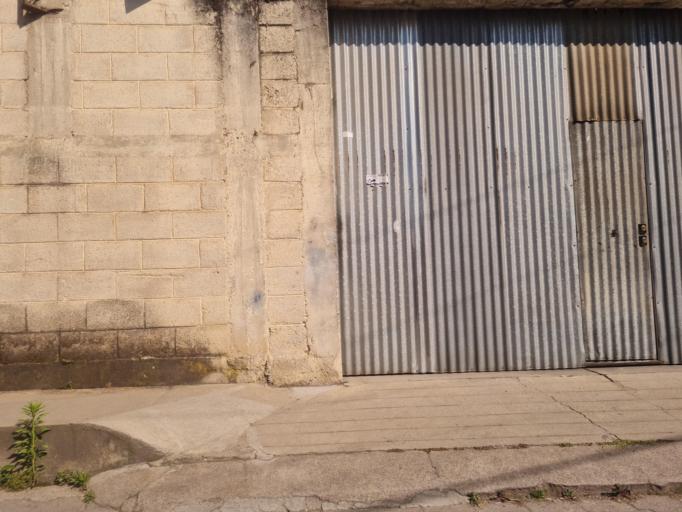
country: GT
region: Quetzaltenango
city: Quetzaltenango
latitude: 14.8411
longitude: -91.5325
